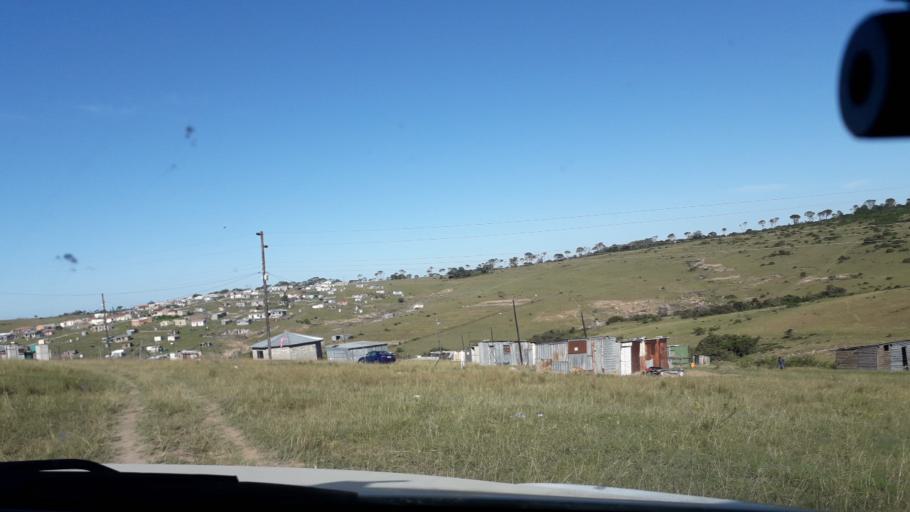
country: ZA
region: Eastern Cape
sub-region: Buffalo City Metropolitan Municipality
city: East London
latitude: -32.8444
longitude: 27.9850
